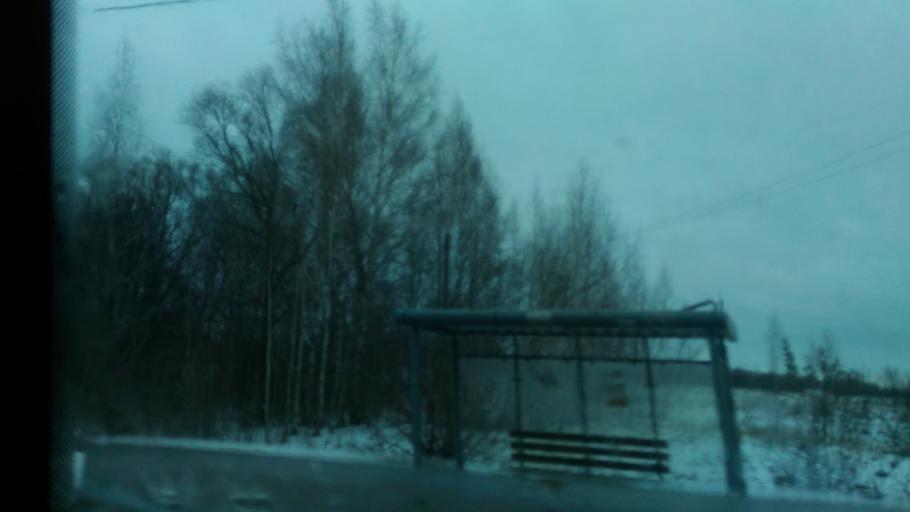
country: RU
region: Tula
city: Bolokhovo
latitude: 54.0530
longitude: 37.8128
